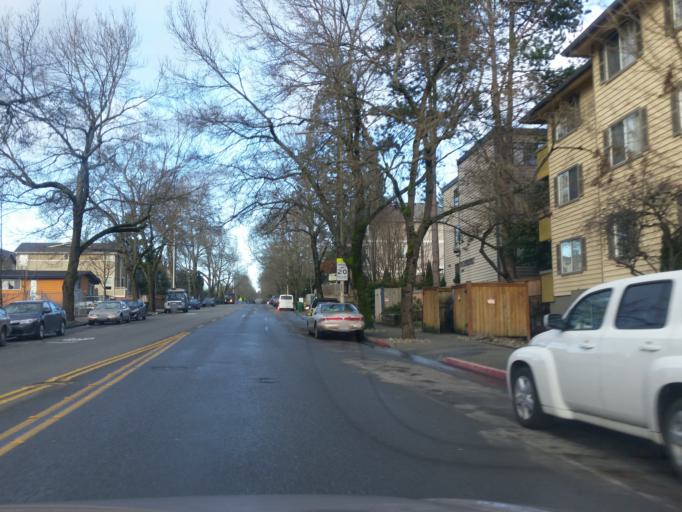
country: US
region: Washington
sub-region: King County
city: Lake Forest Park
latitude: 47.7202
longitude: -122.2908
